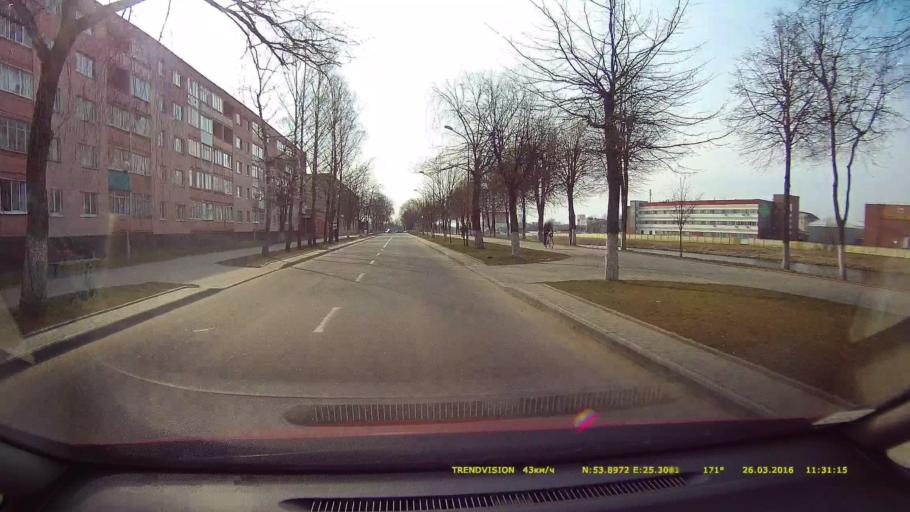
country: BY
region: Grodnenskaya
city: Lida
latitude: 53.8971
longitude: 25.3081
